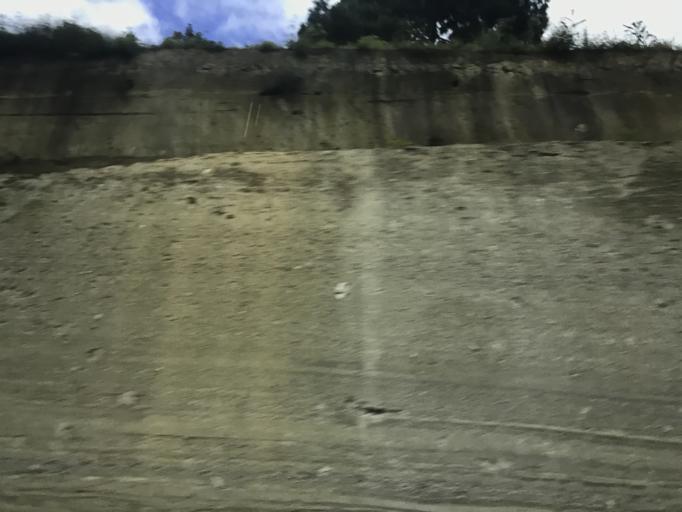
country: GT
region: Chimaltenango
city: Parramos
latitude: 14.6268
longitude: -90.7978
